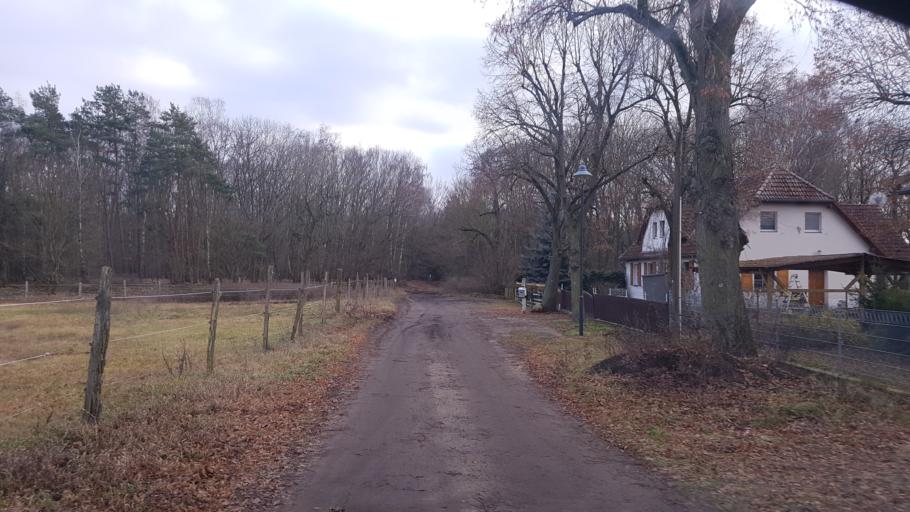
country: DE
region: Brandenburg
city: Ludwigsfelde
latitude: 52.3365
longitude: 13.2214
